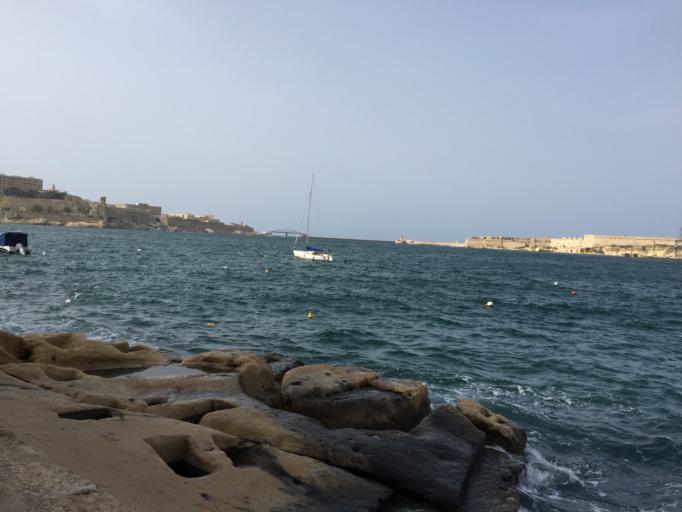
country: MT
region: Il-Birgu
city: Vittoriosa
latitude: 35.8907
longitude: 14.5204
